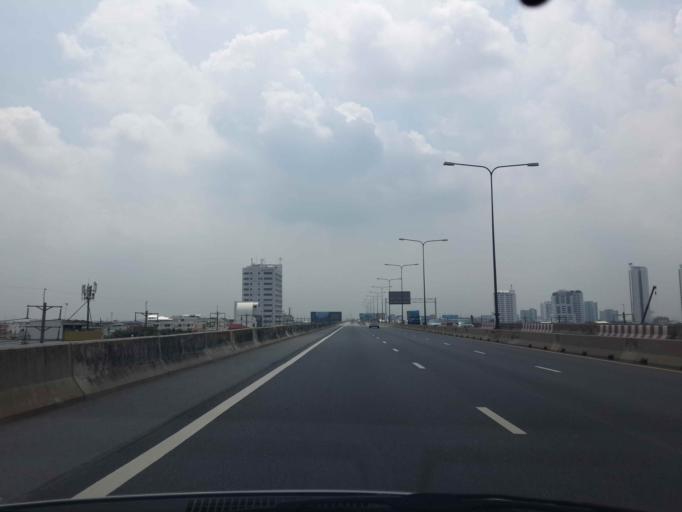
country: TH
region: Bangkok
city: Bang Na
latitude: 13.6644
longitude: 100.6523
